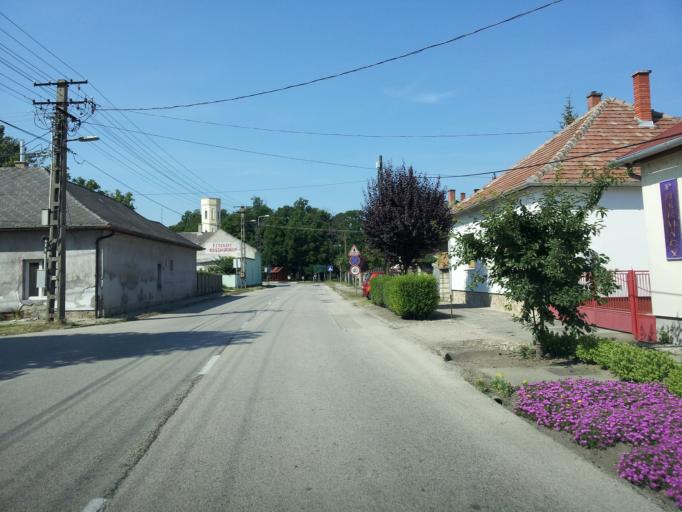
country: HU
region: Fejer
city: Lovasbereny
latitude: 47.3146
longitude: 18.5482
